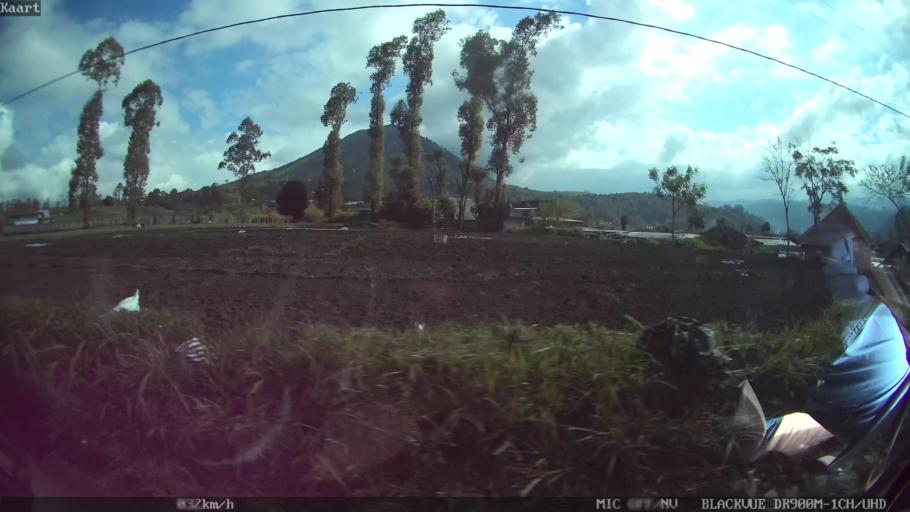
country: ID
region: Bali
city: Banjar Trunyan
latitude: -8.2189
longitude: 115.3928
